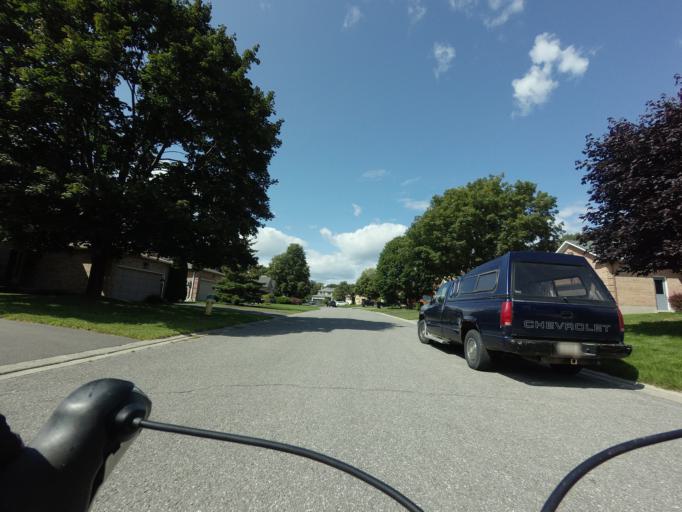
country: CA
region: Ontario
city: Bells Corners
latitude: 45.2900
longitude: -75.8670
